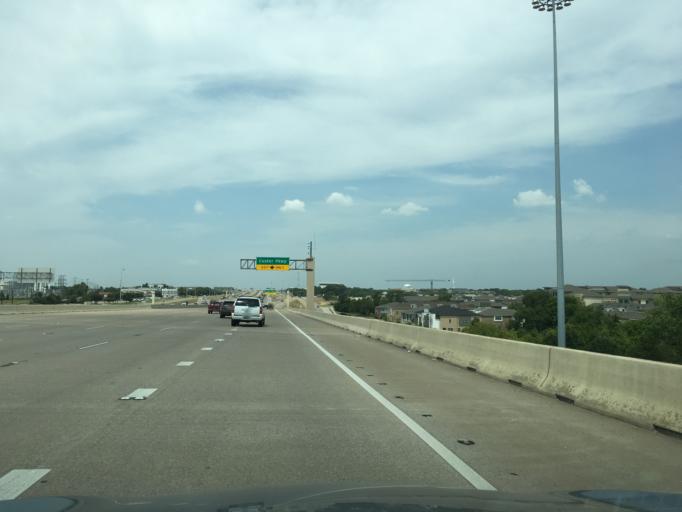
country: US
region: Texas
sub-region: Collin County
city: Plano
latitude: 33.0042
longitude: -96.7159
